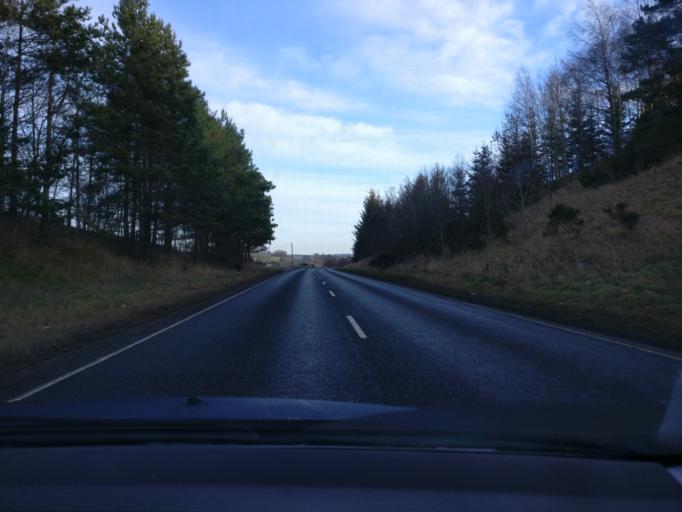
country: GB
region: Scotland
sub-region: The Scottish Borders
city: Hawick
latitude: 55.4462
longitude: -2.7294
